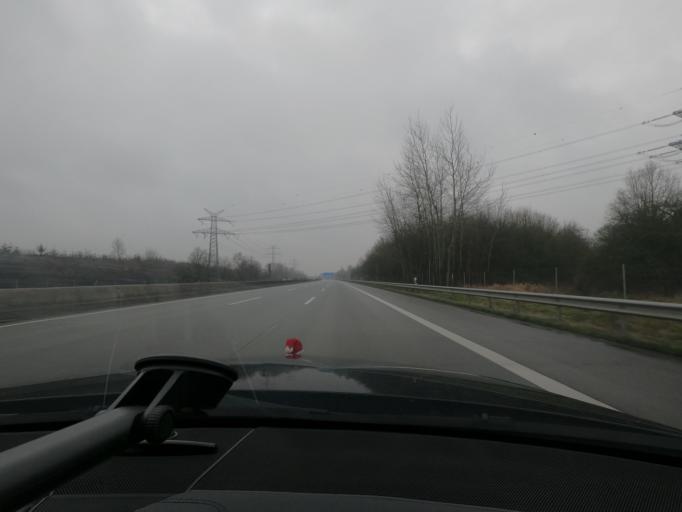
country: DE
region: Schleswig-Holstein
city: Alveslohe
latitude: 53.8117
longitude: 9.9252
